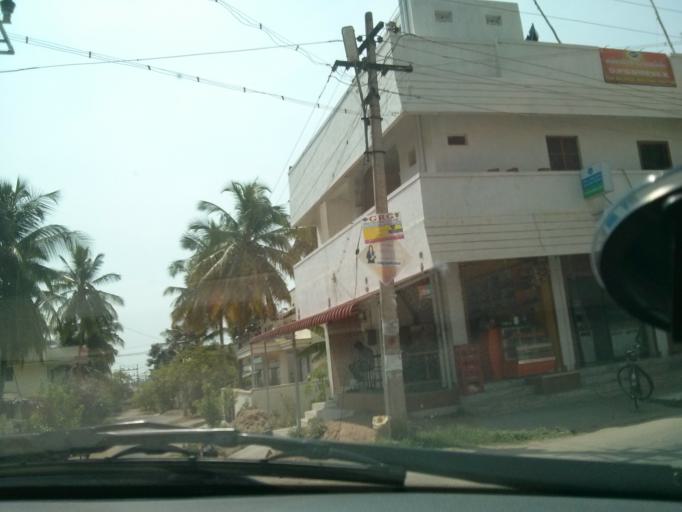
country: IN
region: Tamil Nadu
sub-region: Coimbatore
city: Periyanayakkanpalaiyam
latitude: 11.1549
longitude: 76.9395
